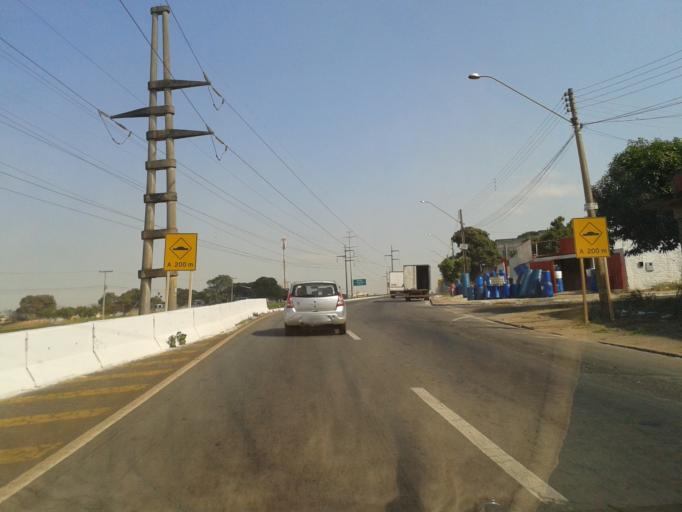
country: BR
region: Goias
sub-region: Aparecida De Goiania
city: Aparecida de Goiania
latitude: -16.7849
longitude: -49.2679
